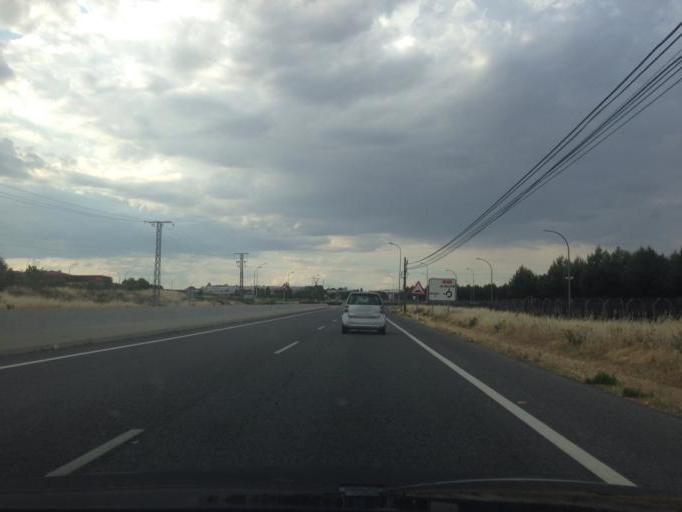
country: ES
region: Madrid
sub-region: Provincia de Madrid
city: Torrejon de Ardoz
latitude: 40.4903
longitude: -3.4784
